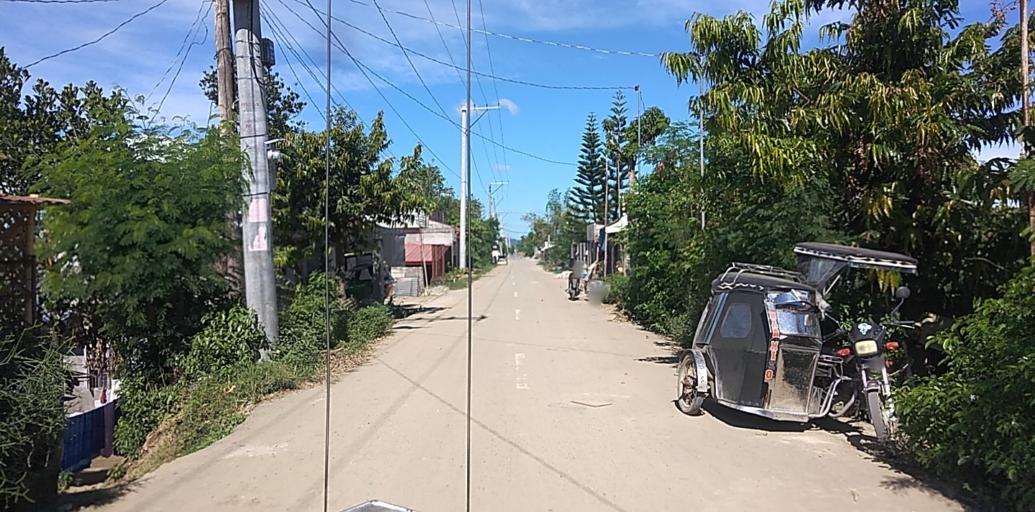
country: PH
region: Central Luzon
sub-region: Province of Pampanga
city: Candating
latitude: 15.1277
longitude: 120.8099
